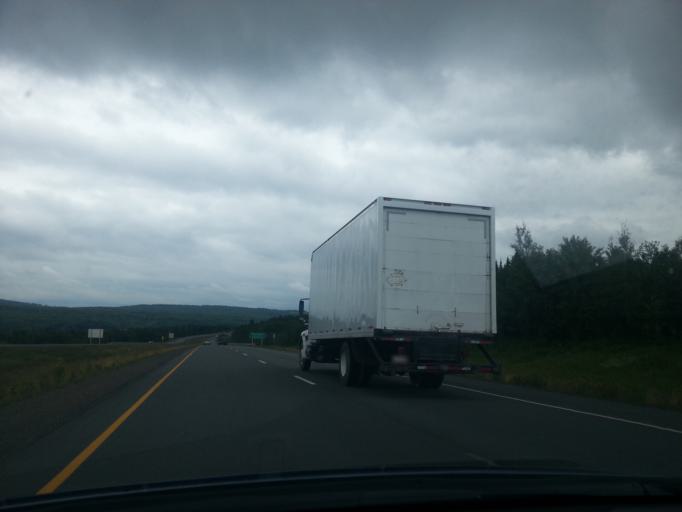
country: CA
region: New Brunswick
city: Harrison Brook
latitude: 47.2199
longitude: -67.9430
